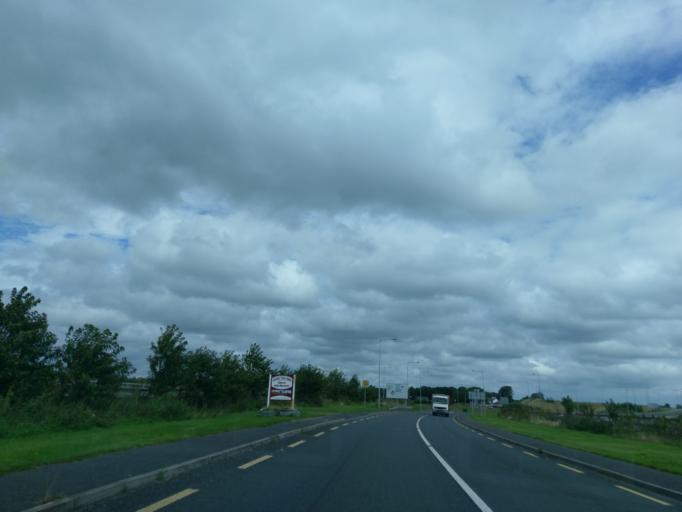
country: IE
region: Connaught
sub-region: County Galway
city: Athenry
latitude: 53.2935
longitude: -8.7644
